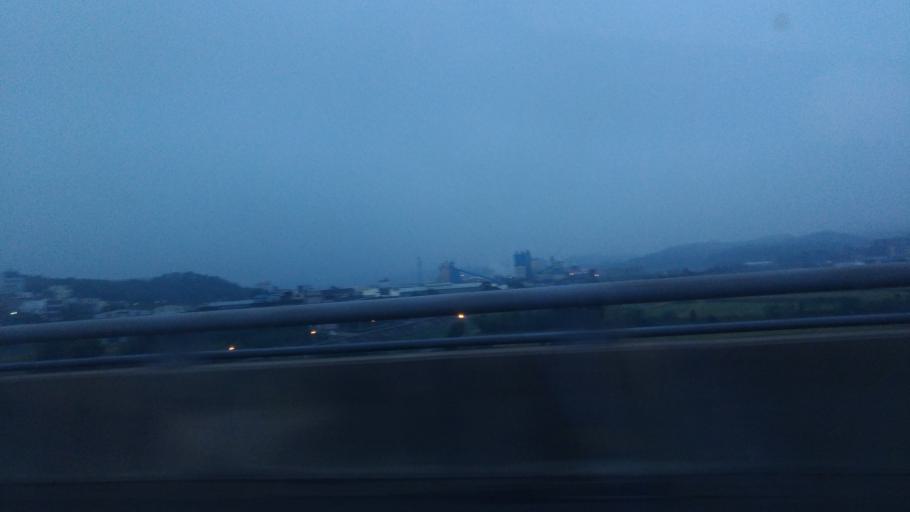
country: TW
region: Taiwan
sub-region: Hsinchu
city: Hsinchu
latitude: 24.7348
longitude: 120.9093
